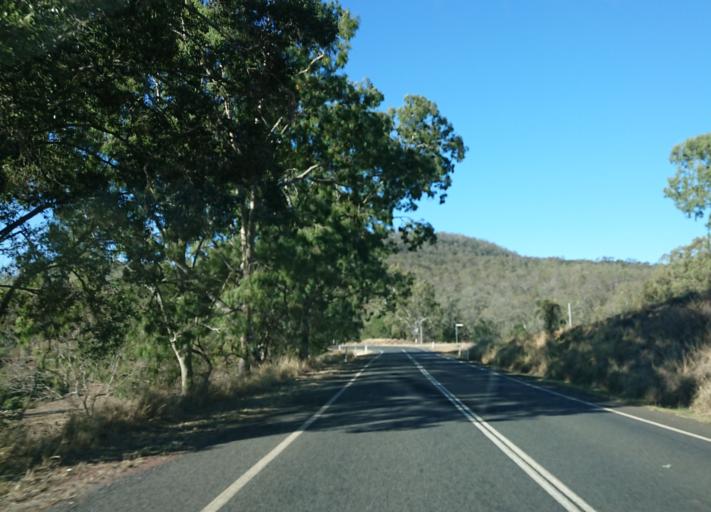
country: AU
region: Queensland
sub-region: Toowoomba
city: Rangeville
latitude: -27.7267
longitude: 152.1151
